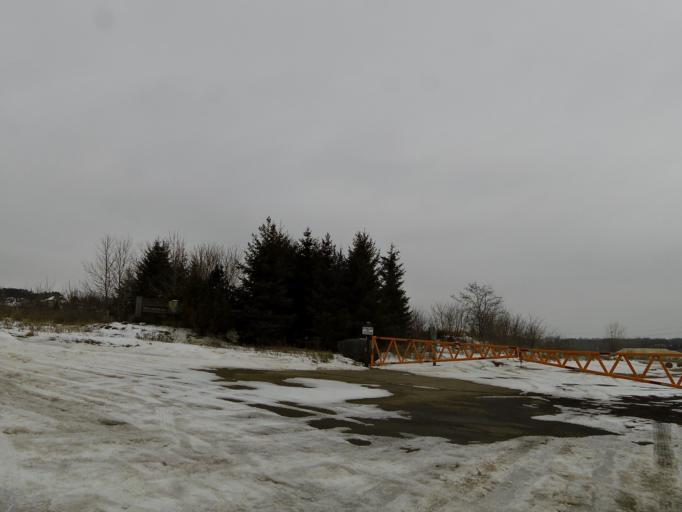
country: US
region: Minnesota
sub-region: Washington County
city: Lakeland
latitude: 44.9540
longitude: -92.8022
